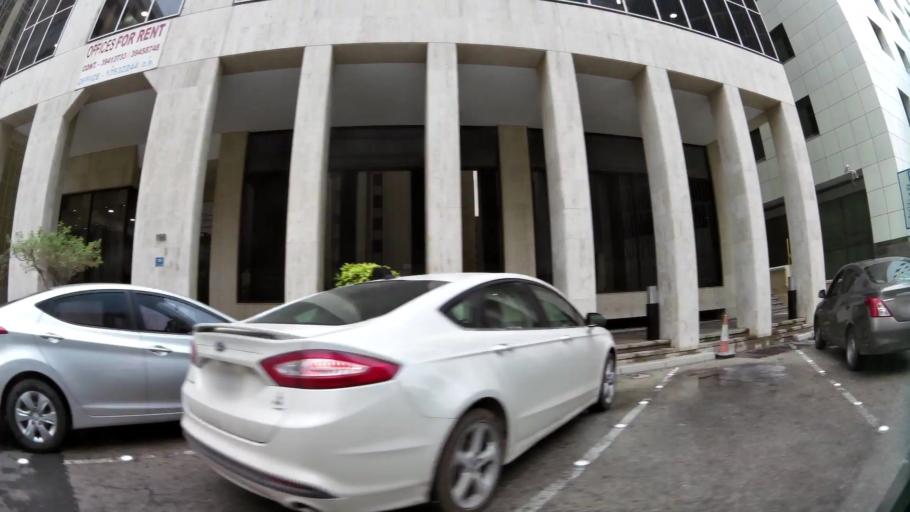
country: BH
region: Muharraq
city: Al Muharraq
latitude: 26.2431
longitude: 50.5889
